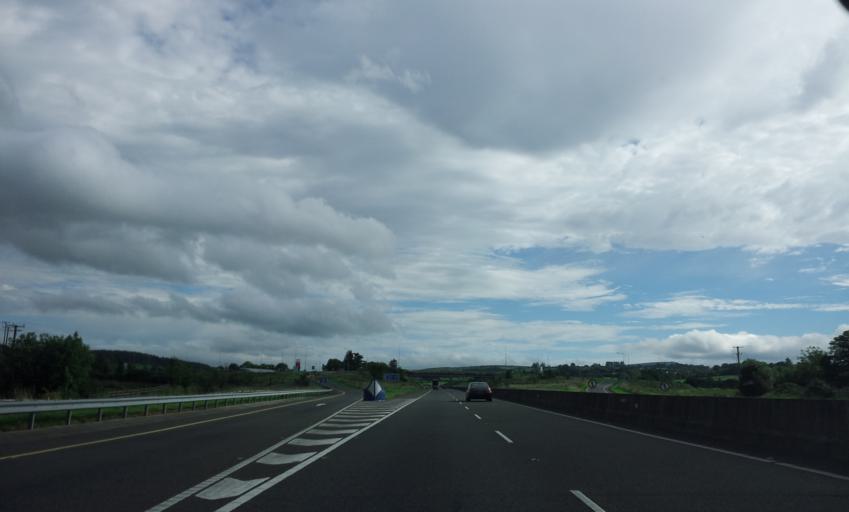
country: IE
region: Munster
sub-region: North Tipperary
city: Newport
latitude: 52.7547
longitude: -8.4150
